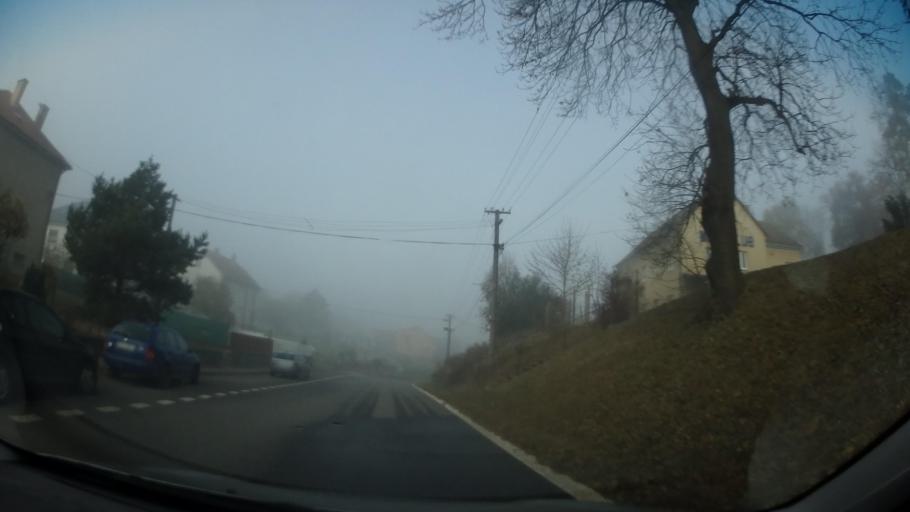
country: CZ
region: Vysocina
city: Krizanov
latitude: 49.4390
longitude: 16.1954
